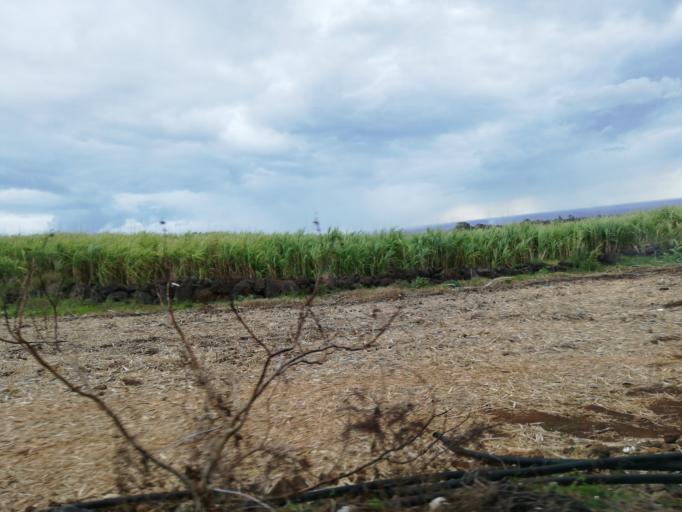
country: MU
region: Black River
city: Petite Riviere
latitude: -20.2102
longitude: 57.4624
